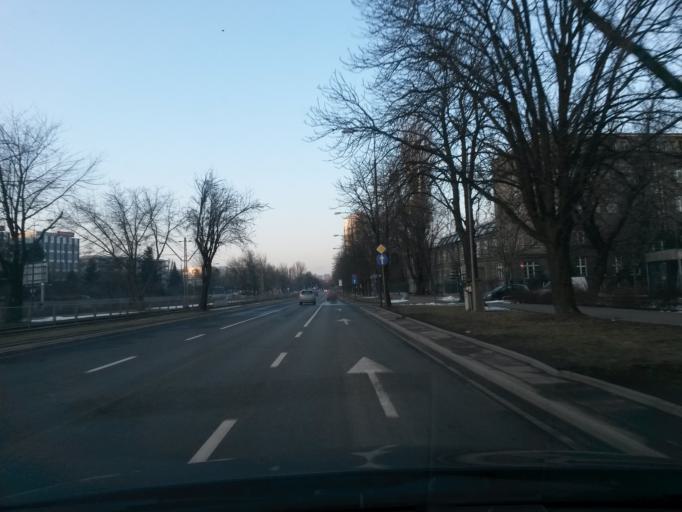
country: PL
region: Masovian Voivodeship
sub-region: Warszawa
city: Ochota
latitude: 52.2031
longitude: 21.0003
